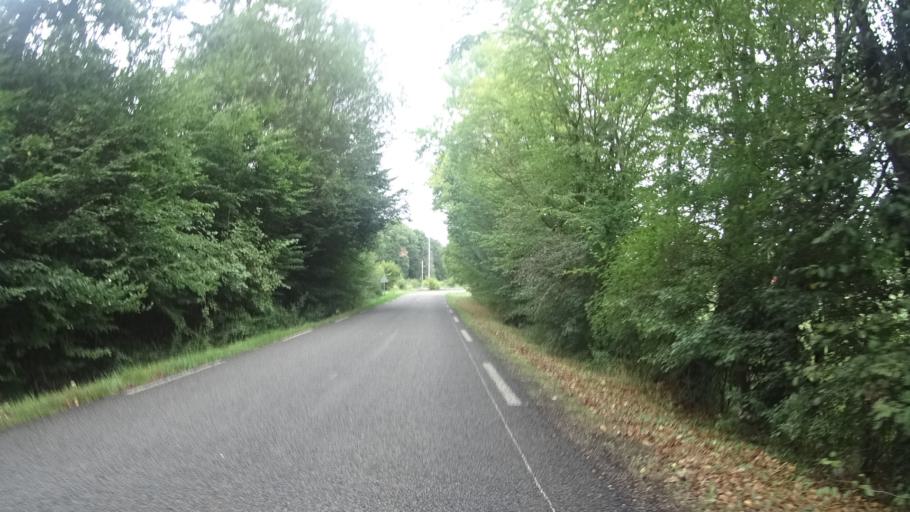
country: FR
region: Nord-Pas-de-Calais
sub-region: Departement du Nord
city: Maroilles
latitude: 50.1684
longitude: 3.7710
